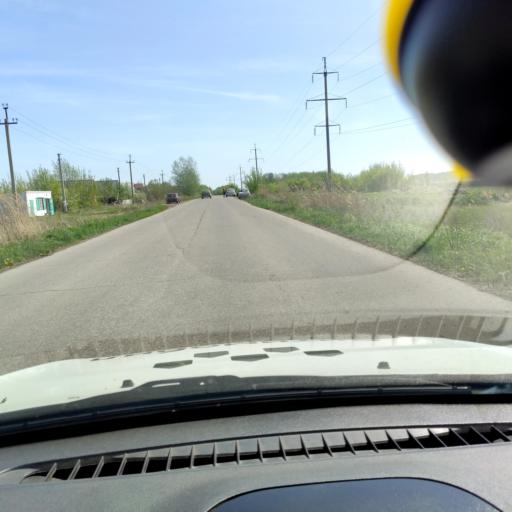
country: RU
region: Samara
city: Tol'yatti
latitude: 53.6632
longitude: 49.3579
